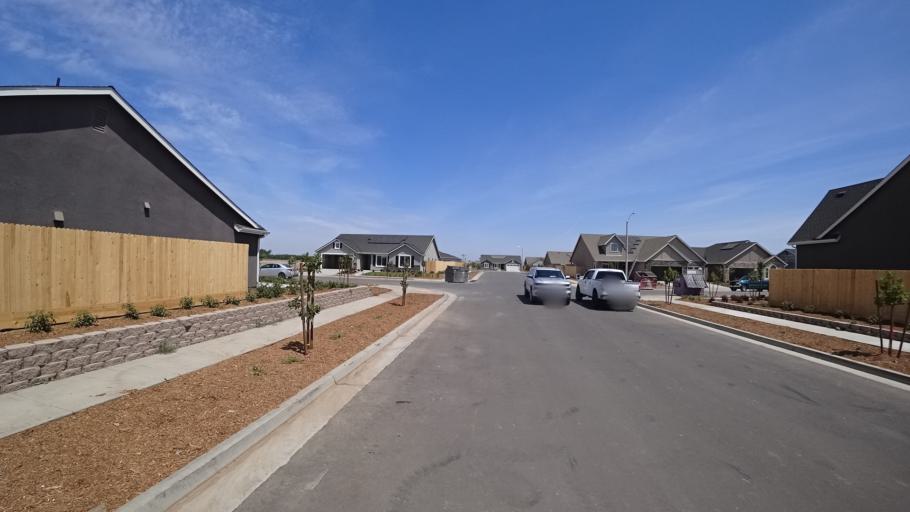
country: US
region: California
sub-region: Kings County
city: Lucerne
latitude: 36.3482
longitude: -119.6854
